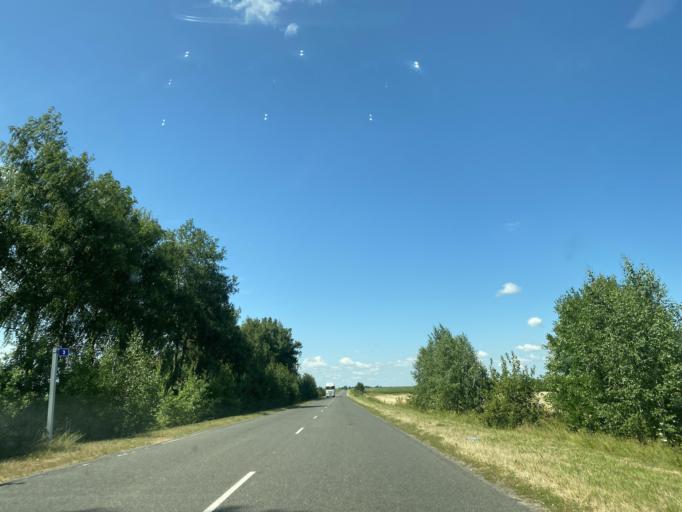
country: BY
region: Brest
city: Ivanava
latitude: 52.1764
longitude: 25.5892
